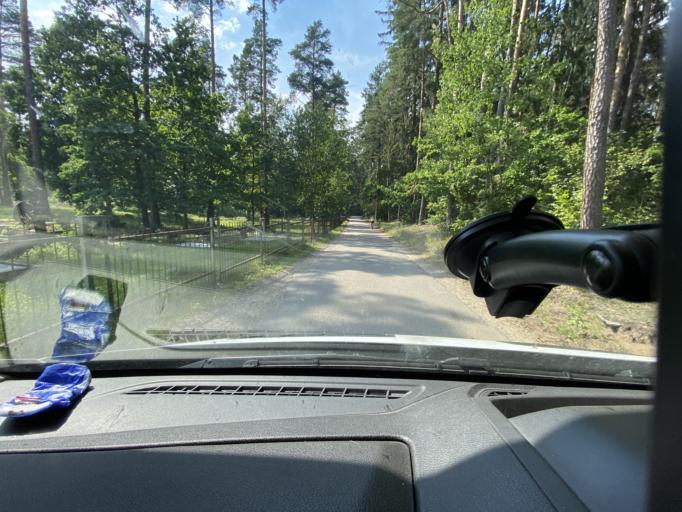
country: LT
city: Ramuciai
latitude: 54.9757
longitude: 24.0397
